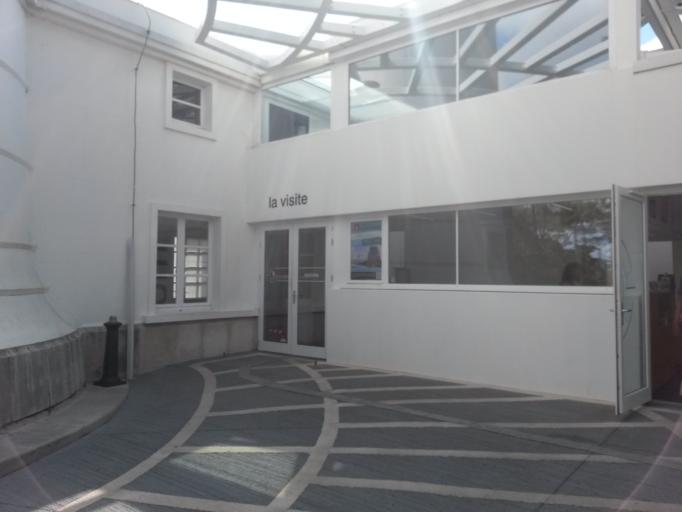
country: FR
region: Aquitaine
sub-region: Departement de la Gironde
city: Arcachon
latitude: 44.6460
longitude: -1.2489
